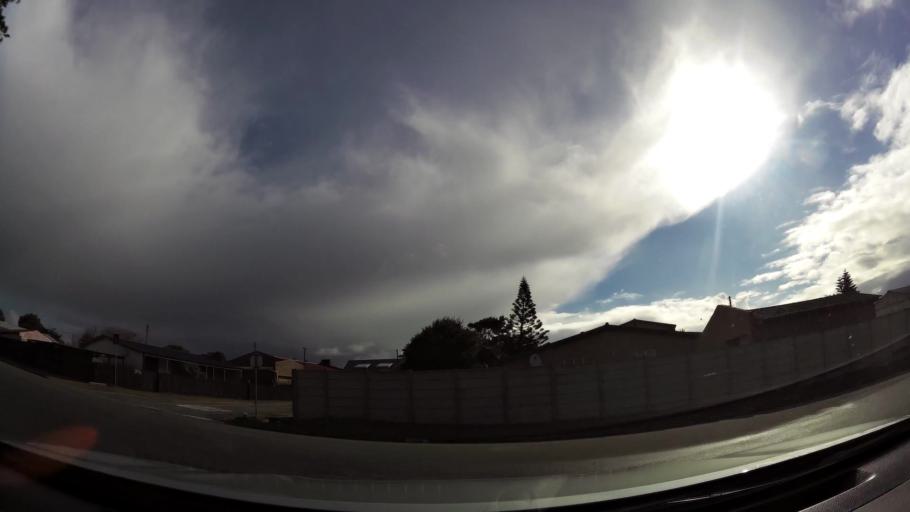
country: ZA
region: Western Cape
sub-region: Eden District Municipality
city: Mossel Bay
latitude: -34.1855
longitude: 22.1273
